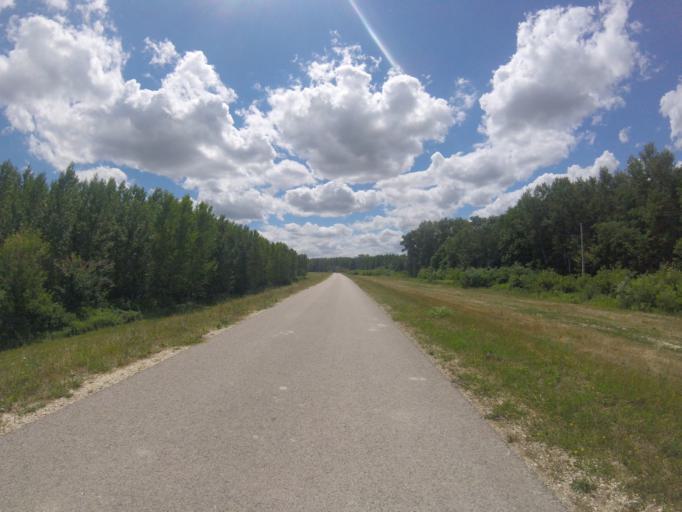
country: HU
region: Tolna
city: Bogyiszlo
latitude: 46.4076
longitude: 18.8800
